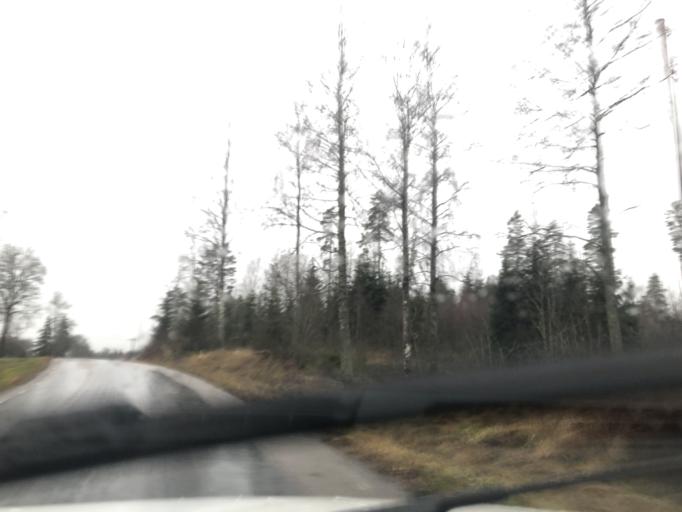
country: SE
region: Vaestra Goetaland
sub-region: Ulricehamns Kommun
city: Ulricehamn
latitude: 57.8351
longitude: 13.5319
